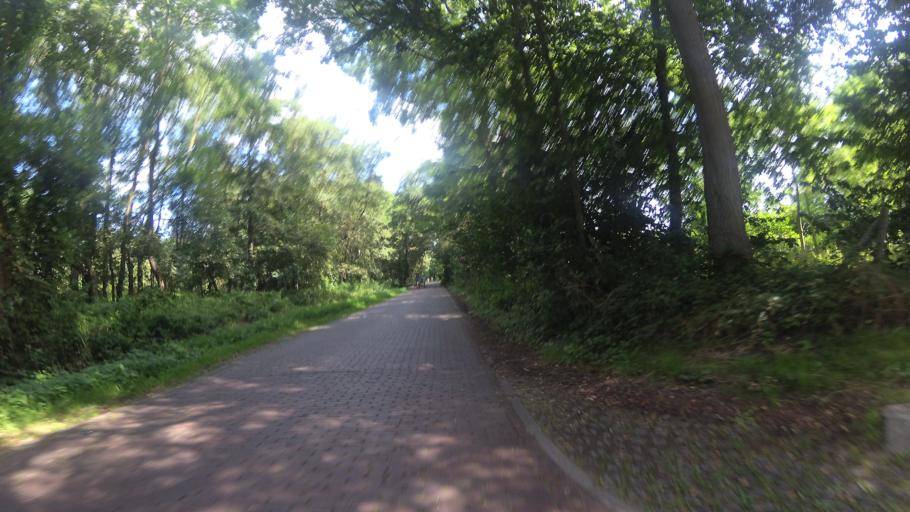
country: NL
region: Zeeland
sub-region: Schouwen-Duiveland
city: Haamstede
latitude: 51.7151
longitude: 3.7538
